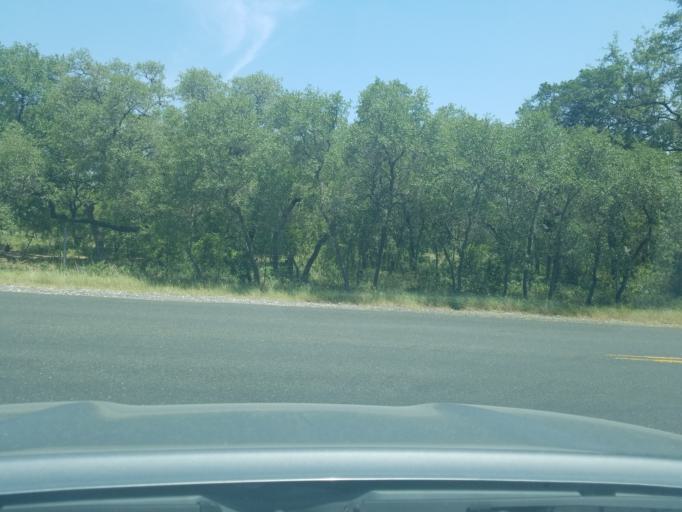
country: US
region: Texas
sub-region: Bexar County
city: Timberwood Park
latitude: 29.6766
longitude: -98.5019
